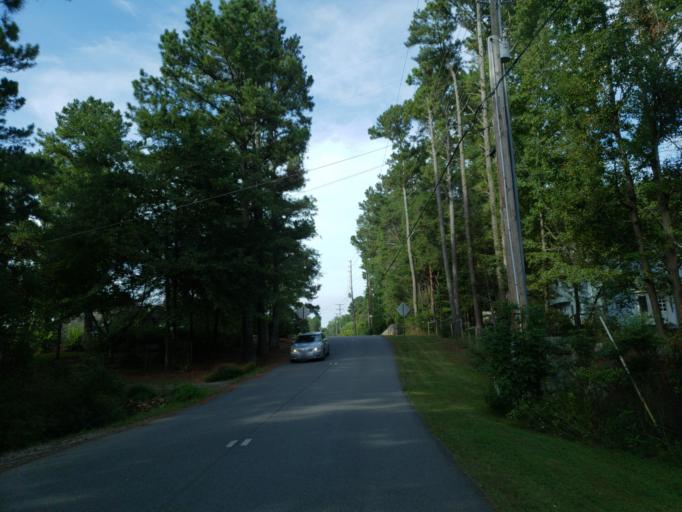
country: US
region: Georgia
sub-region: Cherokee County
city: Woodstock
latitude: 34.0742
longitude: -84.4980
